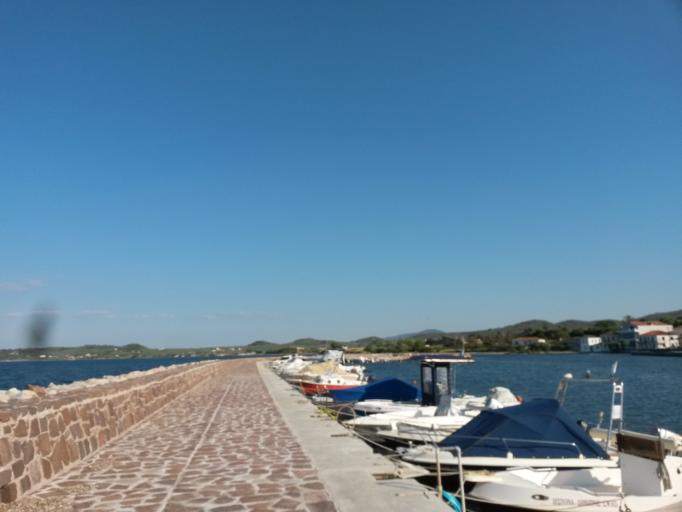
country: GR
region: North Aegean
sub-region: Nomos Lesvou
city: Pamfylla
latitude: 39.1824
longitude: 26.4998
